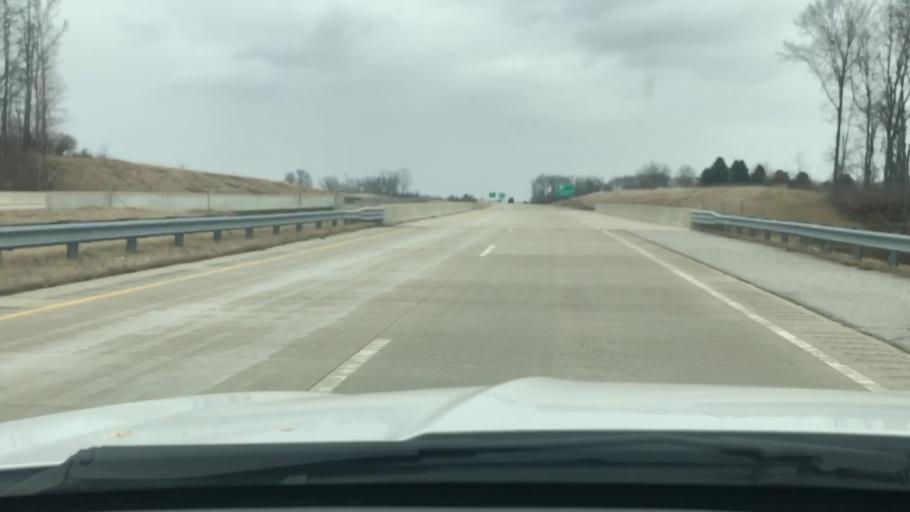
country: US
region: Indiana
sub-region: Cass County
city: Dunkirk
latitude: 40.7272
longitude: -86.3981
